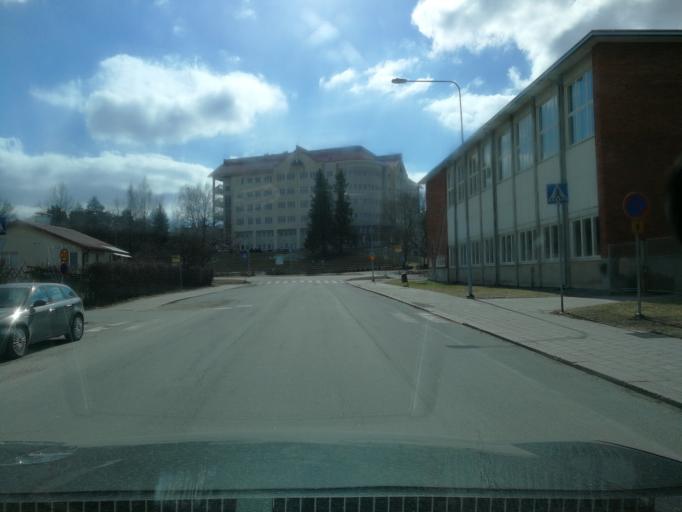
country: FI
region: Varsinais-Suomi
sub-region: Turku
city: Turku
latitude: 60.4417
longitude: 22.2727
